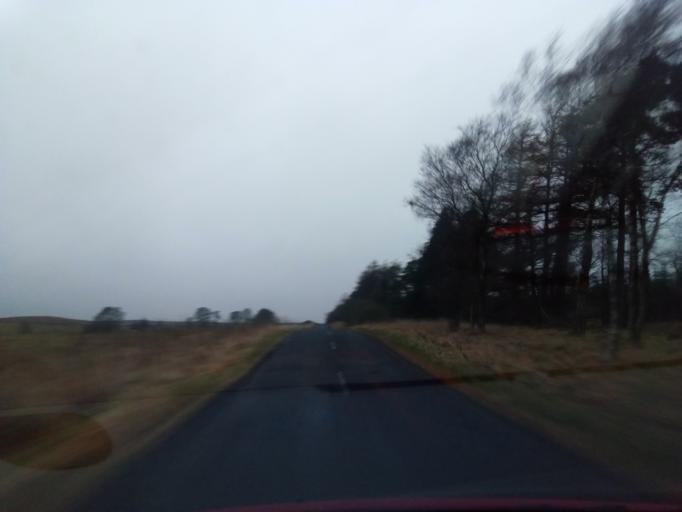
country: GB
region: England
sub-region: Northumberland
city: Rothley
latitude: 55.2083
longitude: -2.0390
